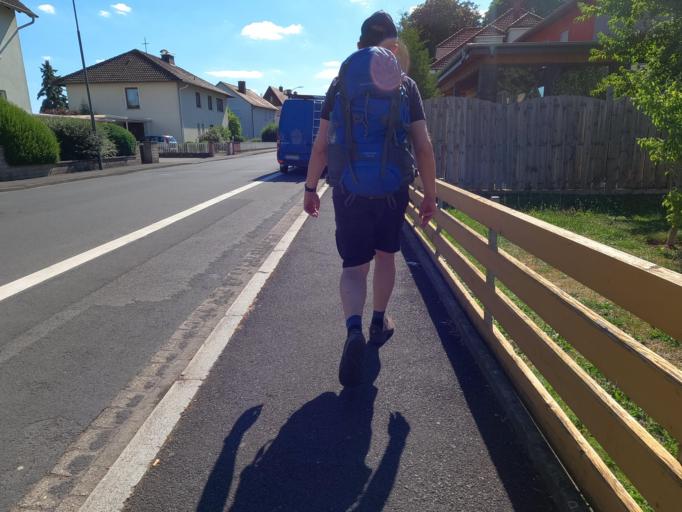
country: DE
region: Hesse
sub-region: Regierungsbezirk Darmstadt
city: Schluchtern
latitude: 50.3507
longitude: 9.5288
